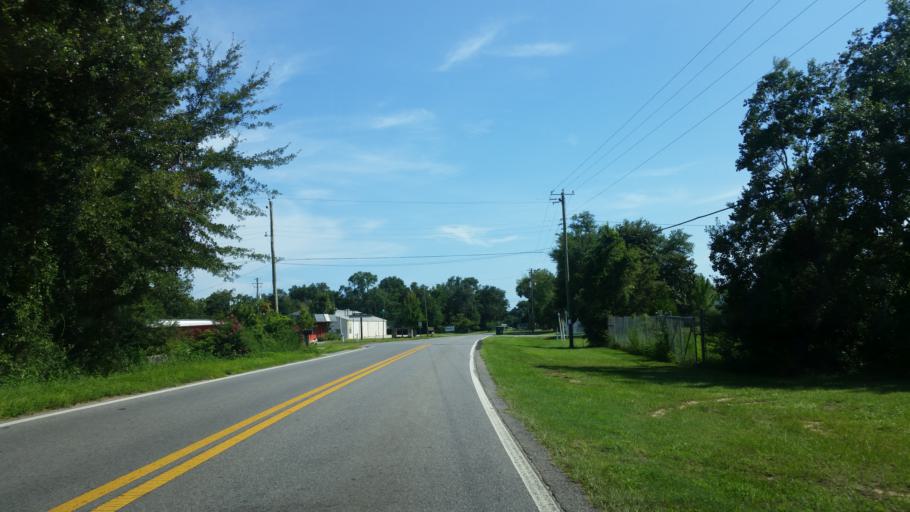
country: US
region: Florida
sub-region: Santa Rosa County
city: Pace
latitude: 30.5973
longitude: -87.1611
